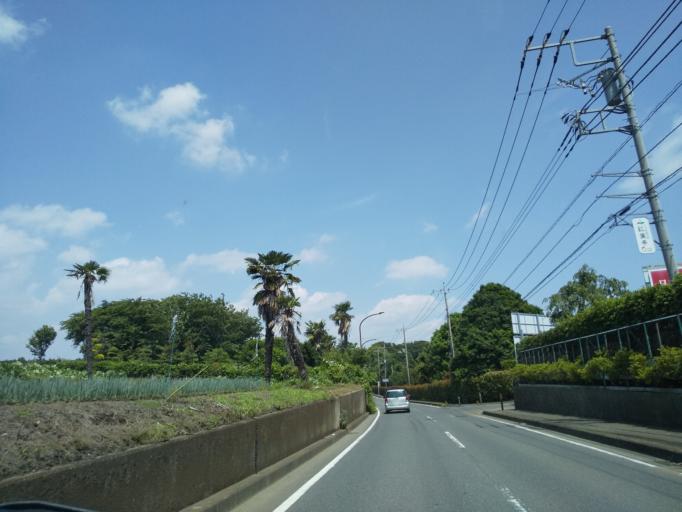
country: JP
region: Kanagawa
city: Zama
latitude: 35.5190
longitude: 139.3898
